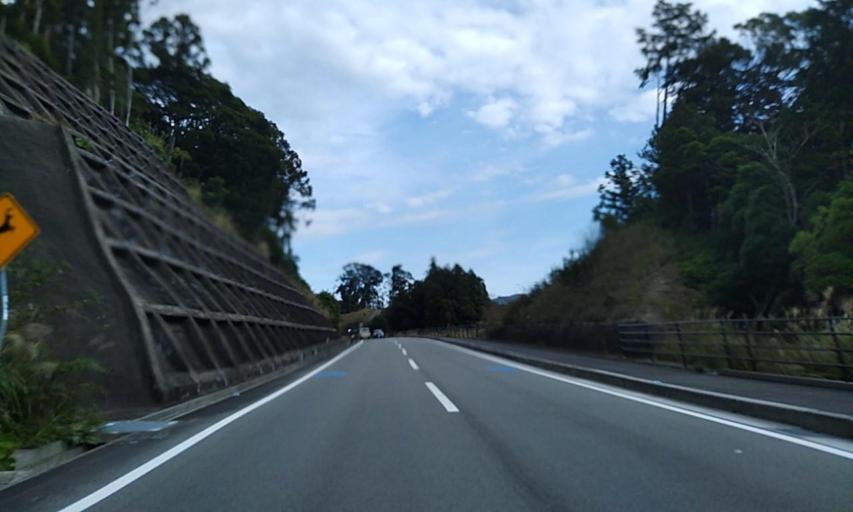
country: JP
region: Mie
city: Ise
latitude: 34.2848
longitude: 136.5534
